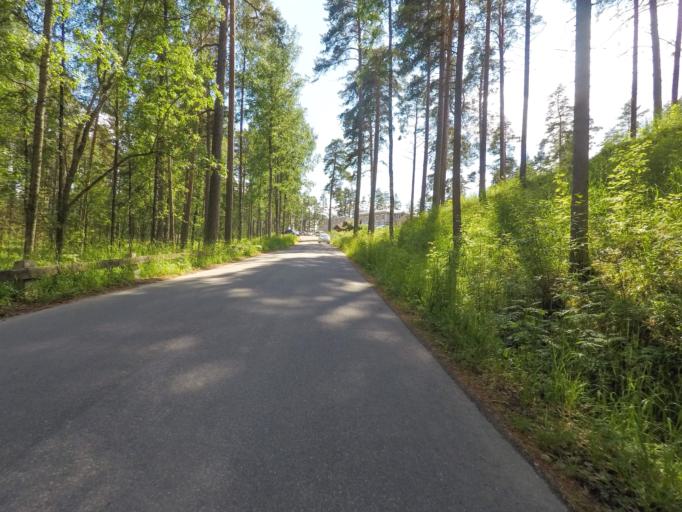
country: FI
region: Southern Savonia
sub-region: Savonlinna
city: Punkaharju
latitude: 61.8022
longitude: 29.3080
